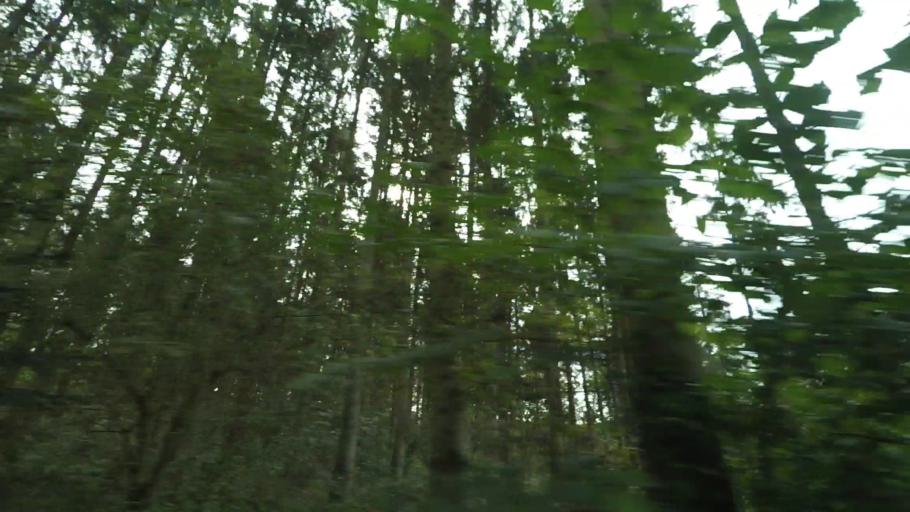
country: DK
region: Central Jutland
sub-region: Syddjurs Kommune
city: Ryomgard
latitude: 56.3453
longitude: 10.4900
